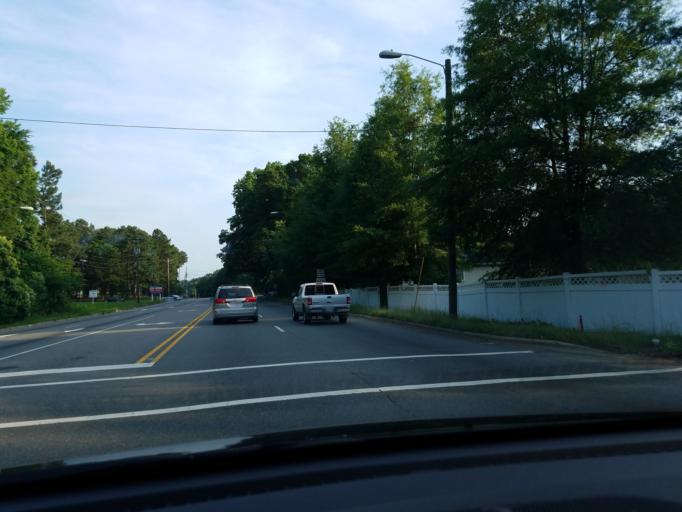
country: US
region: North Carolina
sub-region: Durham County
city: Durham
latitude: 36.0402
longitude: -78.9060
